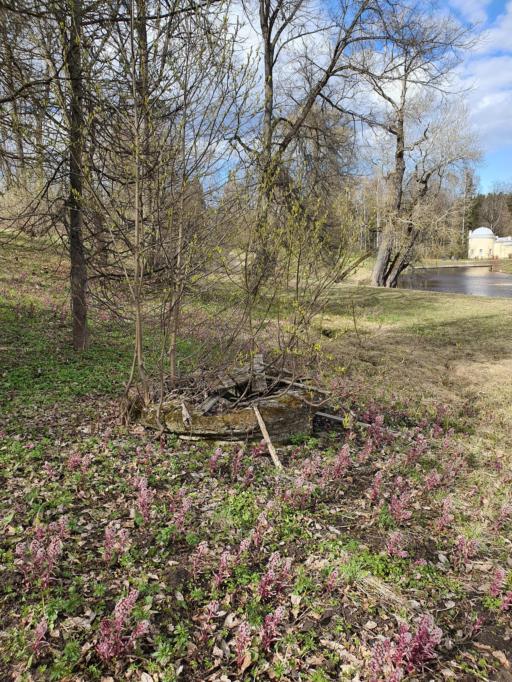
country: RU
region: St.-Petersburg
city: Pavlovsk
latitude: 59.6849
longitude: 30.4489
